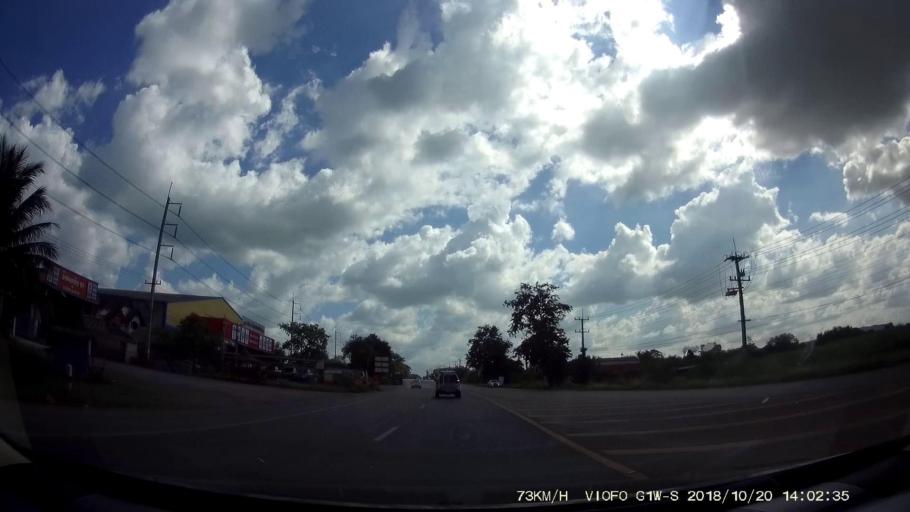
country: TH
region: Khon Kaen
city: Chum Phae
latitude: 16.4901
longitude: 102.1247
